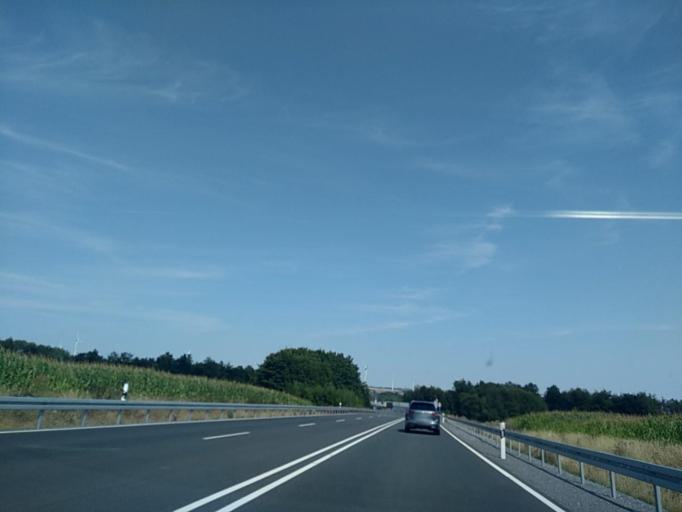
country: DE
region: North Rhine-Westphalia
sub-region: Regierungsbezirk Detmold
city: Wunnenberg
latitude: 51.5114
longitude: 8.6769
